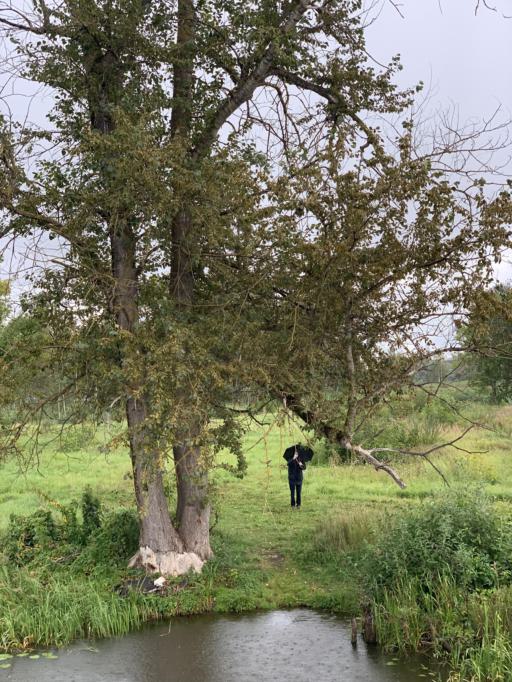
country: RU
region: Tverskaya
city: Vyshniy Volochek
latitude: 57.5811
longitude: 34.5501
